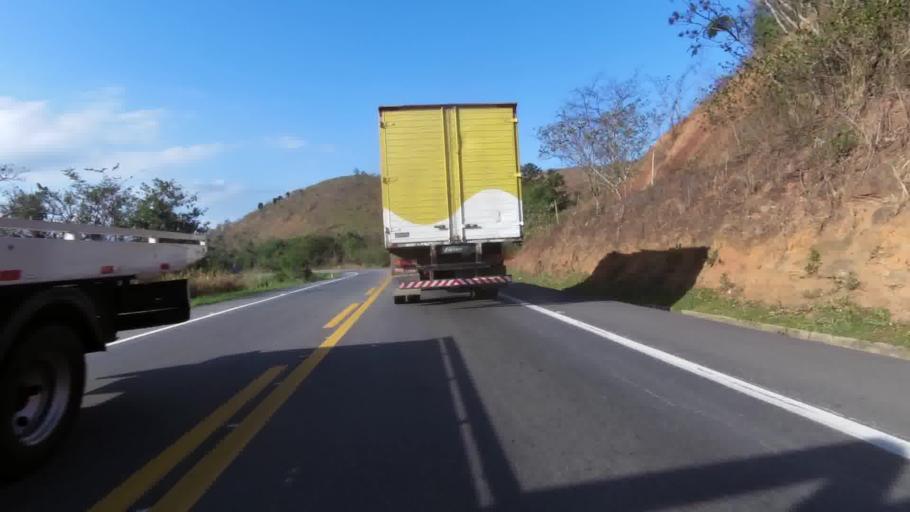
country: BR
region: Espirito Santo
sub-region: Mimoso Do Sul
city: Mimoso do Sul
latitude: -21.1672
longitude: -41.2873
